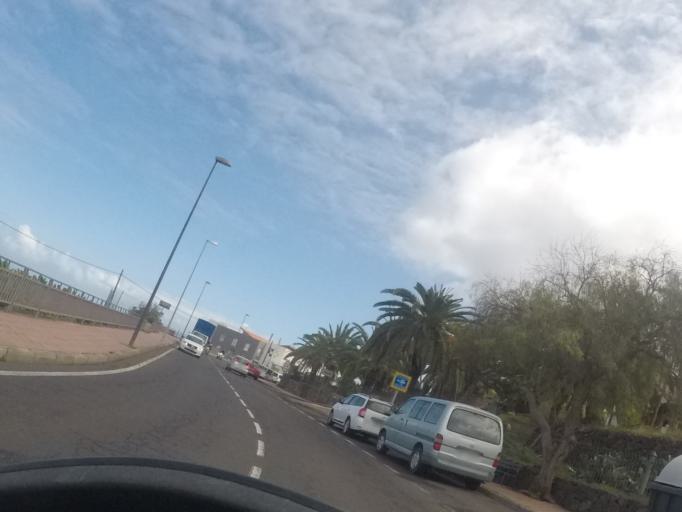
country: ES
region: Canary Islands
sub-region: Provincia de Santa Cruz de Tenerife
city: Tegueste
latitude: 28.5317
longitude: -16.3705
